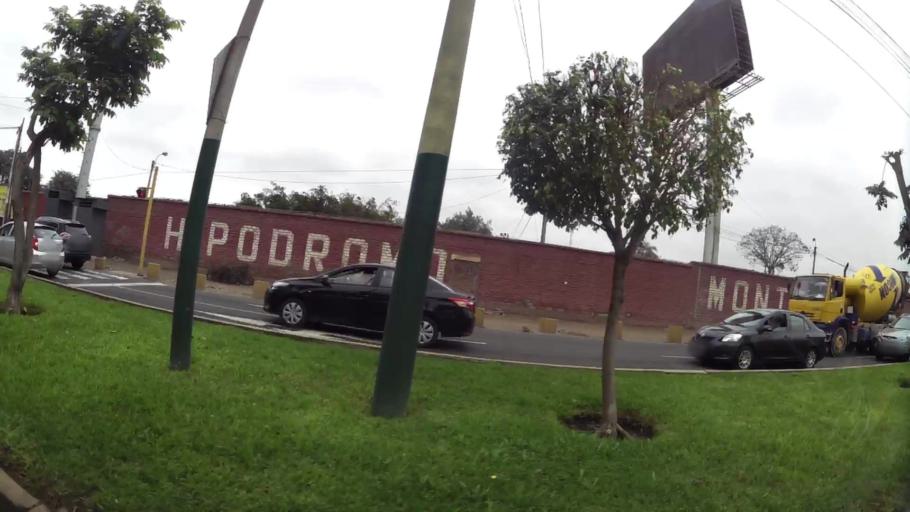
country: PE
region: Lima
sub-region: Lima
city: La Molina
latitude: -12.0905
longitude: -76.9737
